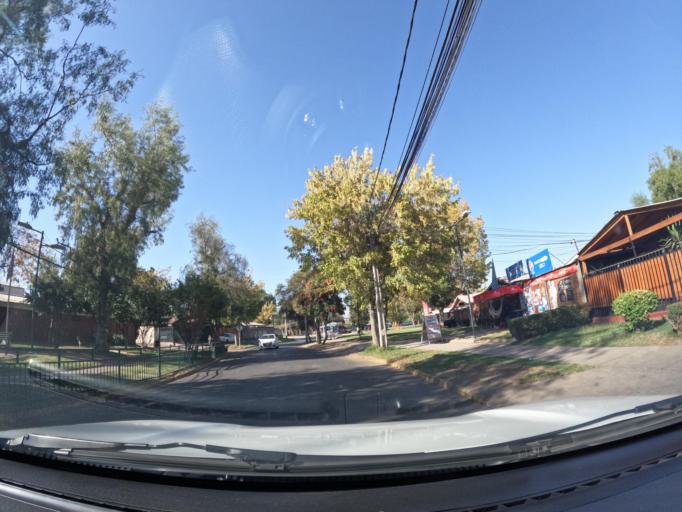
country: CL
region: Santiago Metropolitan
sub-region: Provincia de Santiago
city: Villa Presidente Frei, Nunoa, Santiago, Chile
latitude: -33.5012
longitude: -70.5784
